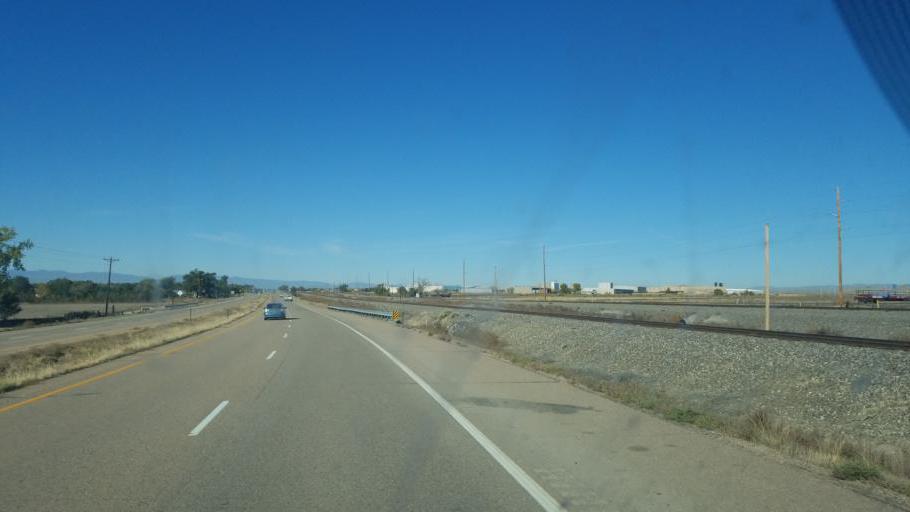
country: US
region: Colorado
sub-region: Pueblo County
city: Pueblo
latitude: 38.2759
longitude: -104.4723
